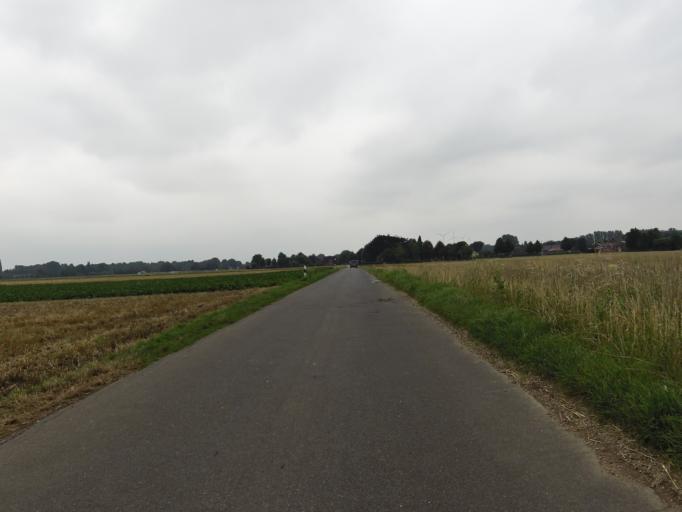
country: DE
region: North Rhine-Westphalia
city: Geilenkirchen
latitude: 50.9980
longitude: 6.1781
